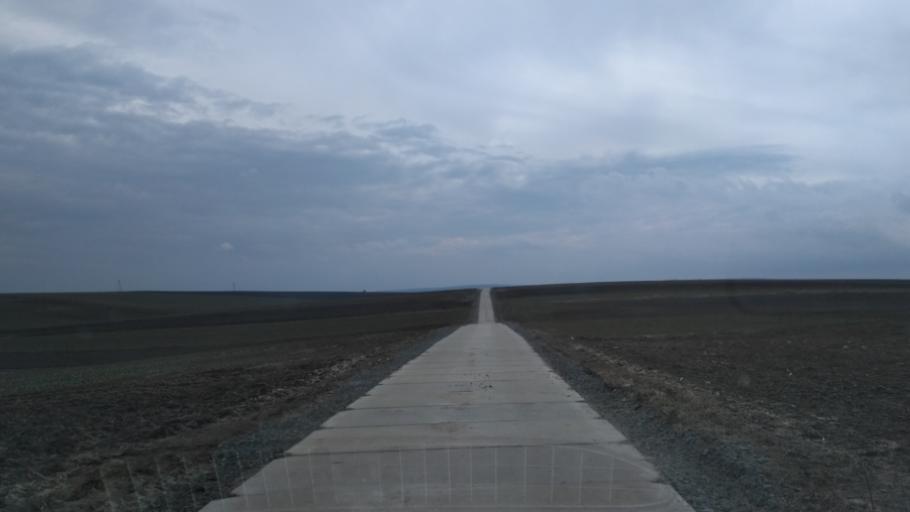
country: PL
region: Subcarpathian Voivodeship
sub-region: Powiat jaroslawski
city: Rokietnica
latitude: 49.9353
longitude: 22.5909
